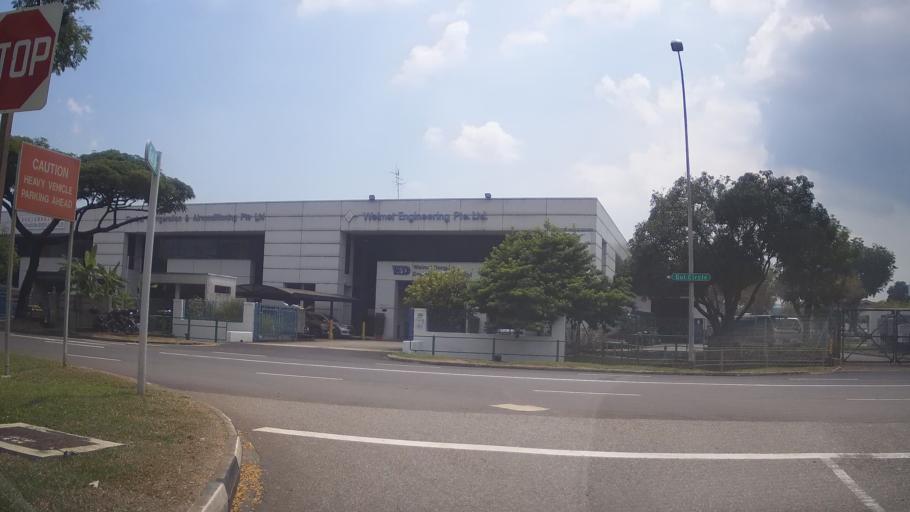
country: MY
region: Johor
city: Johor Bahru
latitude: 1.3151
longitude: 103.6634
